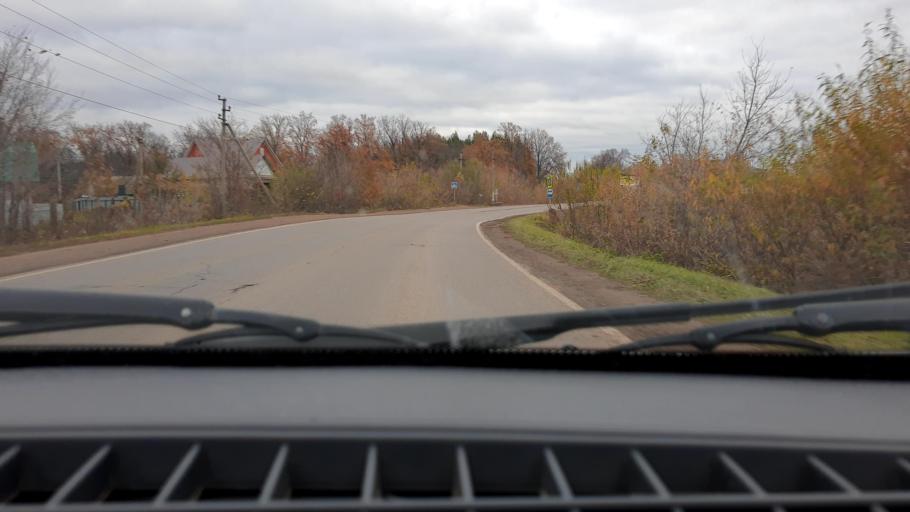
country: RU
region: Bashkortostan
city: Ufa
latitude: 54.5635
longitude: 55.9519
